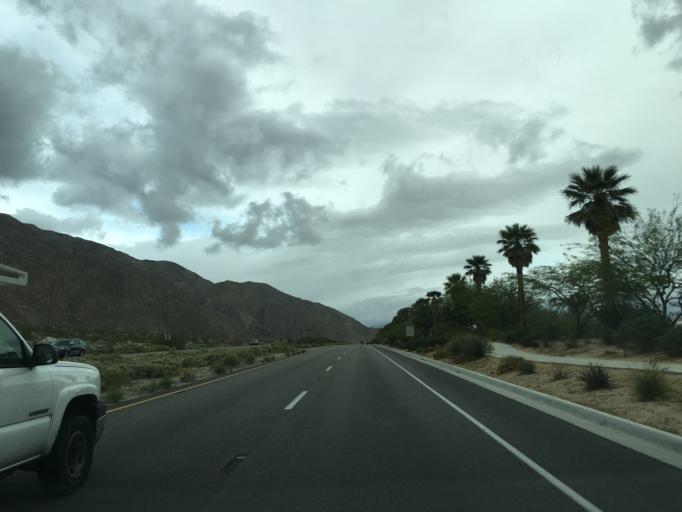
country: US
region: California
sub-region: Riverside County
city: Palm Springs
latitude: 33.8626
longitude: -116.5634
